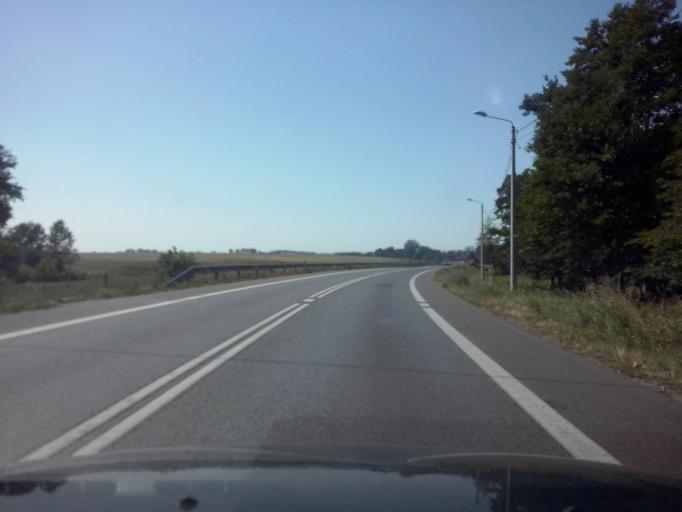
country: PL
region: Swietokrzyskie
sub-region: Powiat kielecki
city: Wola Jachowa
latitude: 50.8486
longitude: 20.8990
